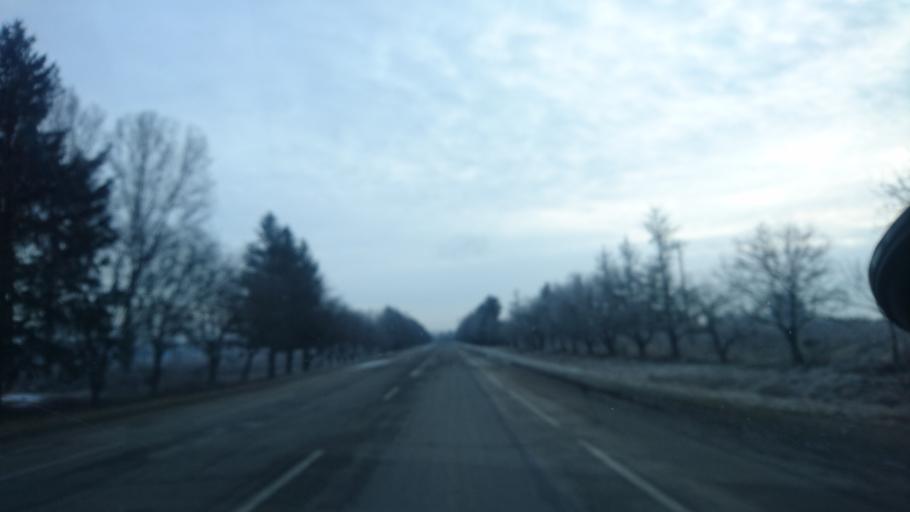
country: MD
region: Briceni
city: Briceni
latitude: 48.3028
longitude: 27.1243
